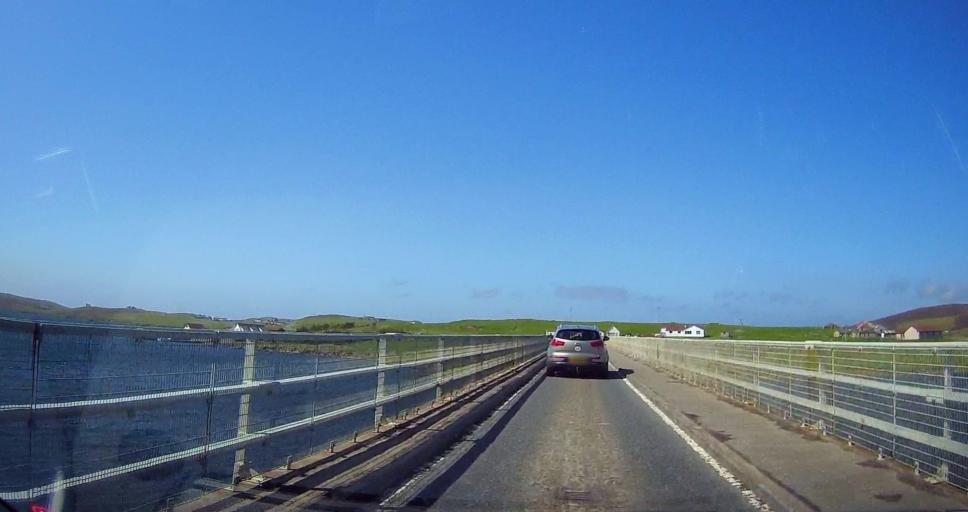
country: GB
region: Scotland
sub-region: Shetland Islands
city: Lerwick
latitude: 60.1291
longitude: -1.2709
